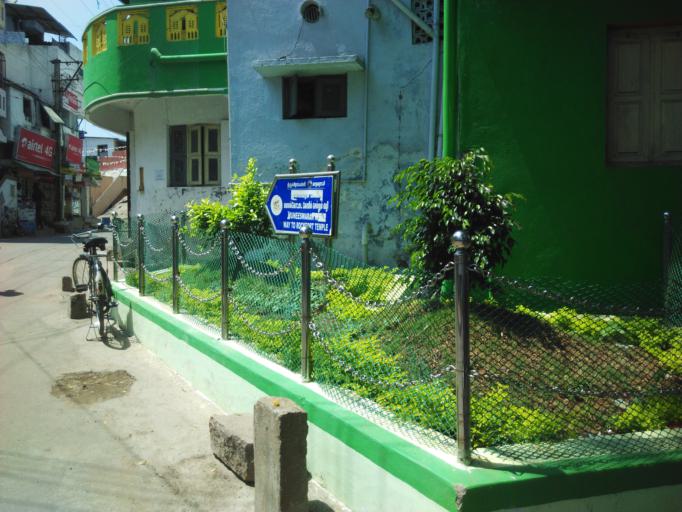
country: IN
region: Tamil Nadu
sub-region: Tiruchchirappalli
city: Tiruchirappalli
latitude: 10.8277
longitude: 78.6986
